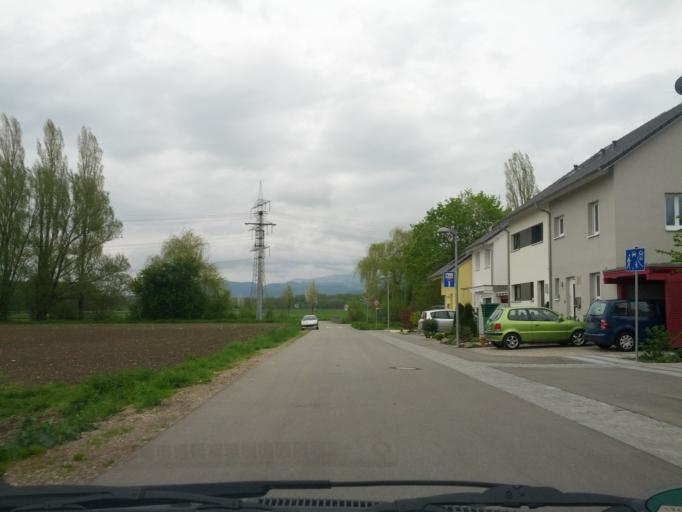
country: DE
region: Baden-Wuerttemberg
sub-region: Freiburg Region
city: Merdingen
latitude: 48.0043
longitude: 7.7223
